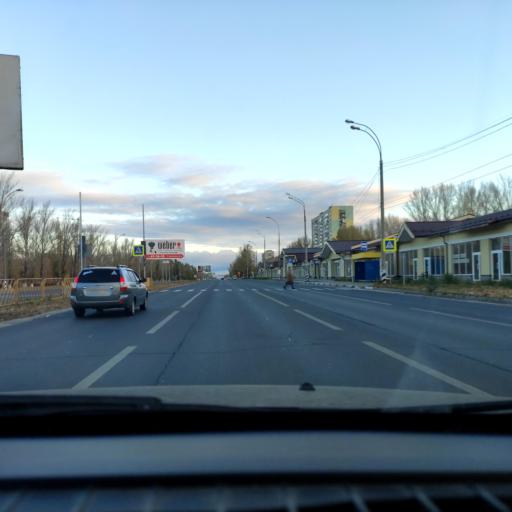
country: RU
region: Samara
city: Tol'yatti
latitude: 53.5216
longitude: 49.2799
